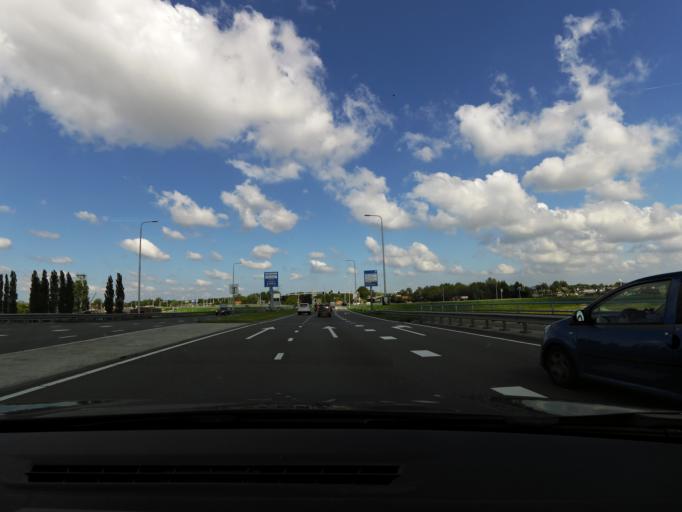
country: NL
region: South Holland
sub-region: Gemeente Alphen aan den Rijn
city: Alphen aan den Rijn
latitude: 52.1137
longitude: 4.6765
